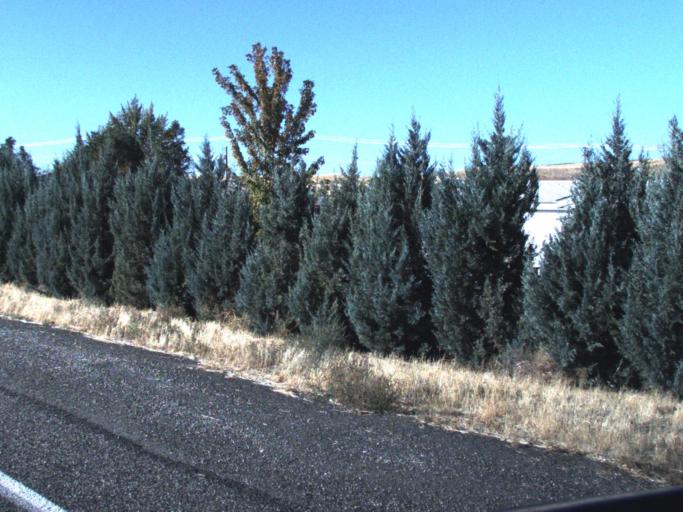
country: US
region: Washington
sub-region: Benton County
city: West Richland
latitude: 46.2945
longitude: -119.3861
